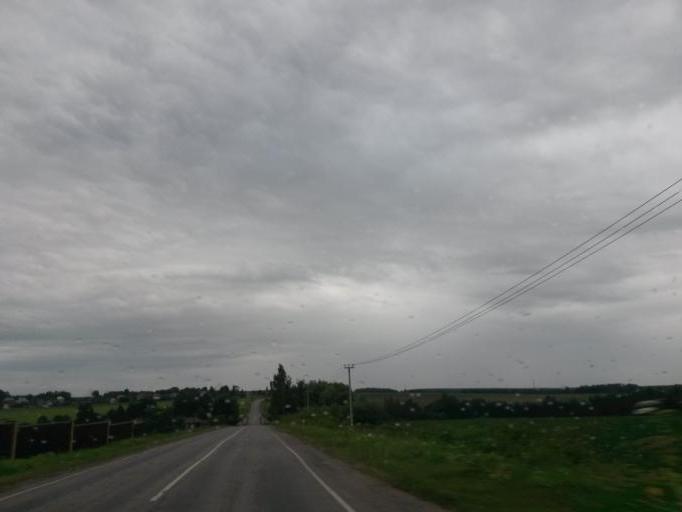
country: RU
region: Moskovskaya
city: Barybino
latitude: 55.2371
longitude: 37.7969
